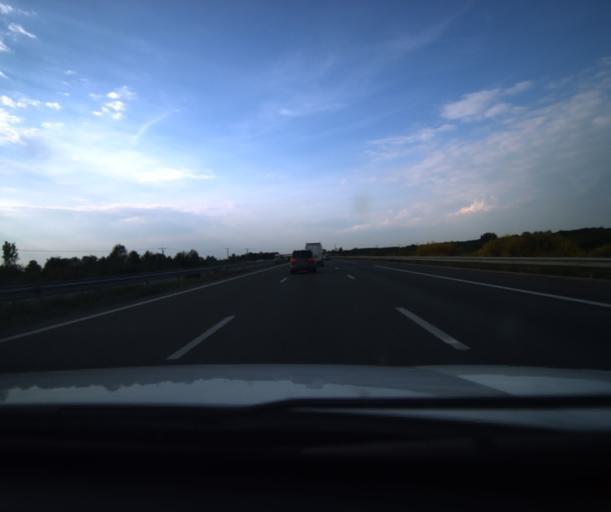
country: FR
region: Midi-Pyrenees
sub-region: Departement du Tarn-et-Garonne
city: Campsas
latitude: 43.8680
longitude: 1.3187
